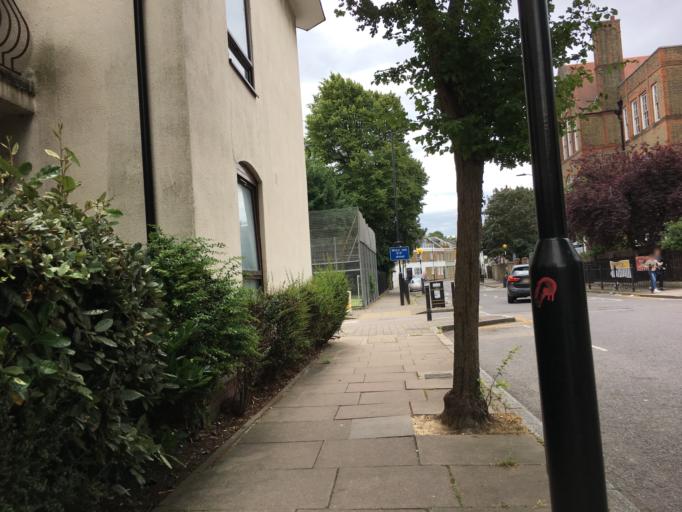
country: GB
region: England
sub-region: Greater London
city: Barnsbury
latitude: 51.5412
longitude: -0.1095
